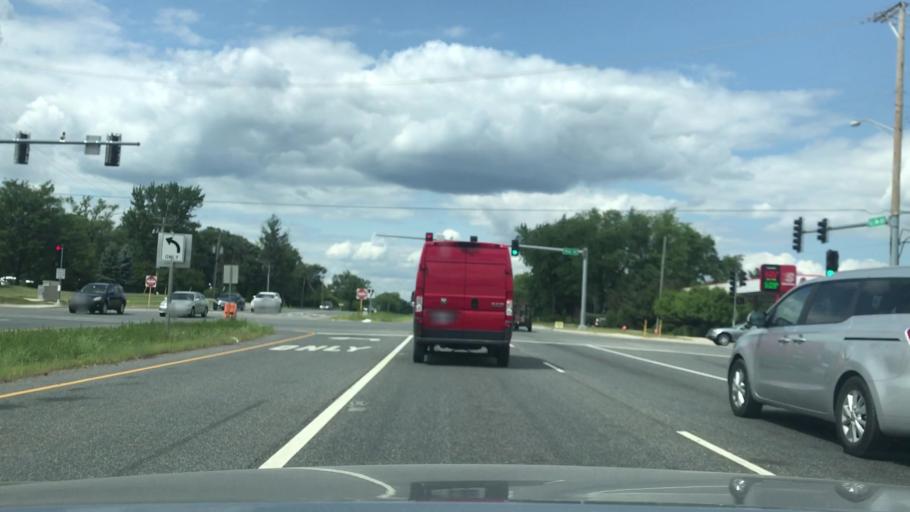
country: US
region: Illinois
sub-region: DuPage County
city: Burr Ridge
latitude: 41.7229
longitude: -87.9437
